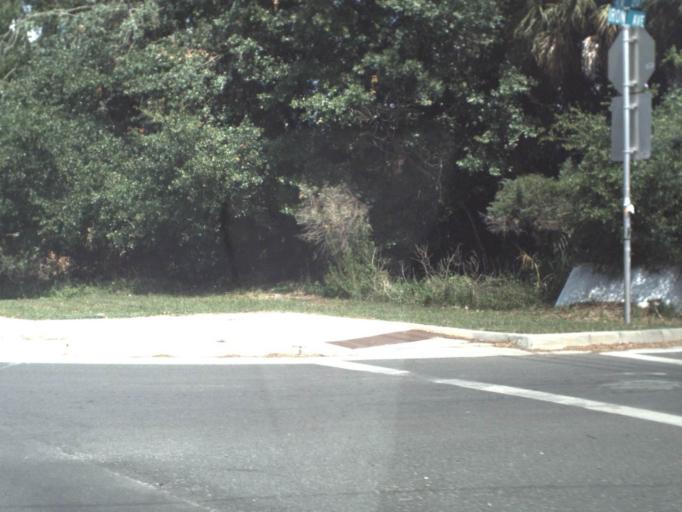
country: US
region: Florida
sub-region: Putnam County
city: Interlachen
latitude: 29.6280
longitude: -81.8438
